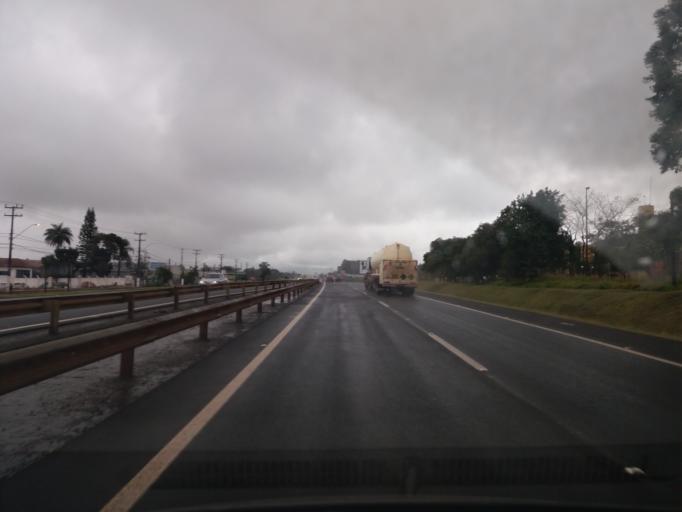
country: BR
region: Parana
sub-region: Cascavel
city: Cascavel
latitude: -24.9947
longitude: -53.5136
